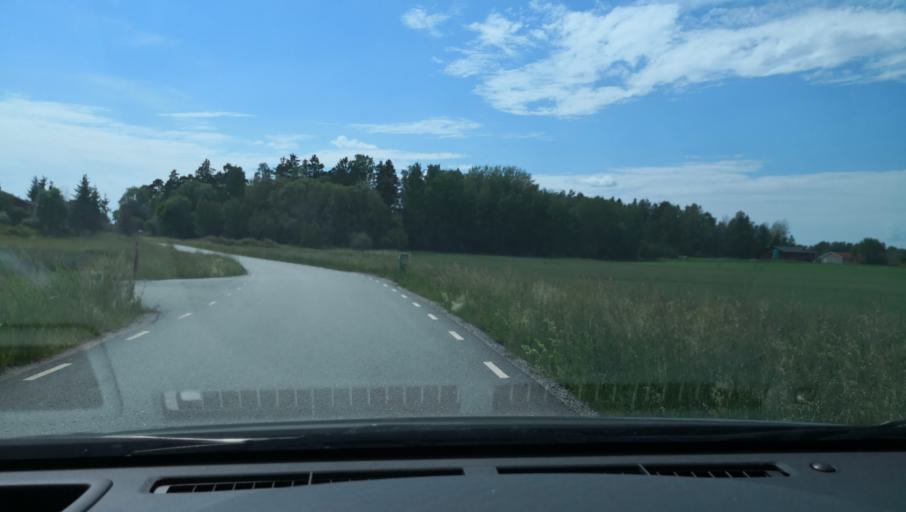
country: SE
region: Uppsala
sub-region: Habo Kommun
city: Balsta
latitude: 59.6901
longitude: 17.4662
